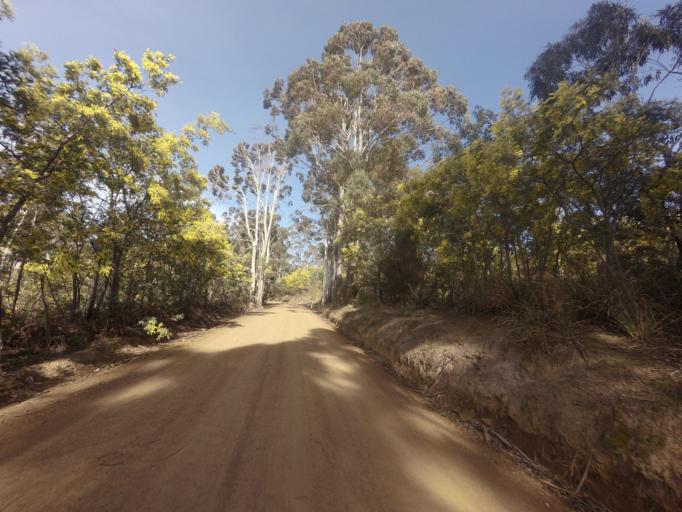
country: AU
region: Tasmania
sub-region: Kingborough
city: Kettering
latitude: -43.0897
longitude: 147.2657
